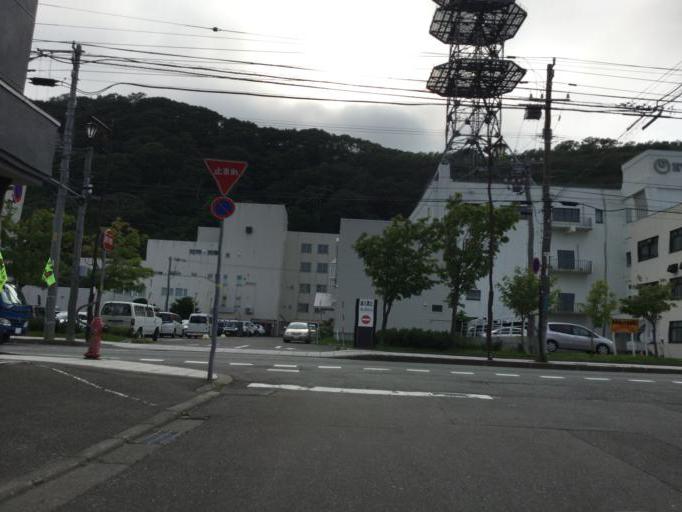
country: JP
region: Hokkaido
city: Wakkanai
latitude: 45.4140
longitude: 141.6744
